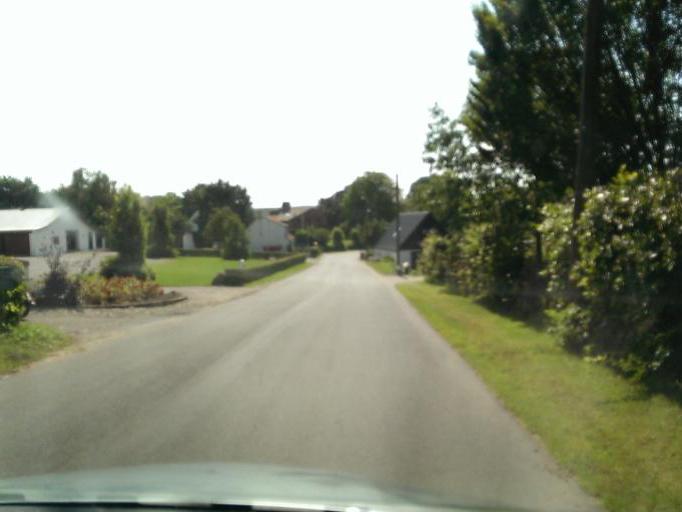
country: DK
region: Central Jutland
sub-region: Syddjurs Kommune
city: Ronde
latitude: 56.2684
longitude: 10.5551
